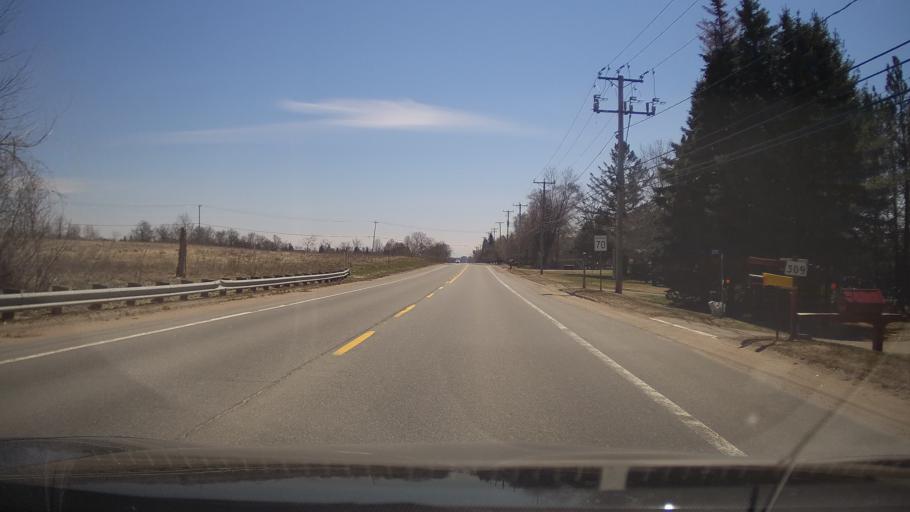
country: CA
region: Ontario
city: Bells Corners
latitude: 45.4157
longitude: -75.8803
